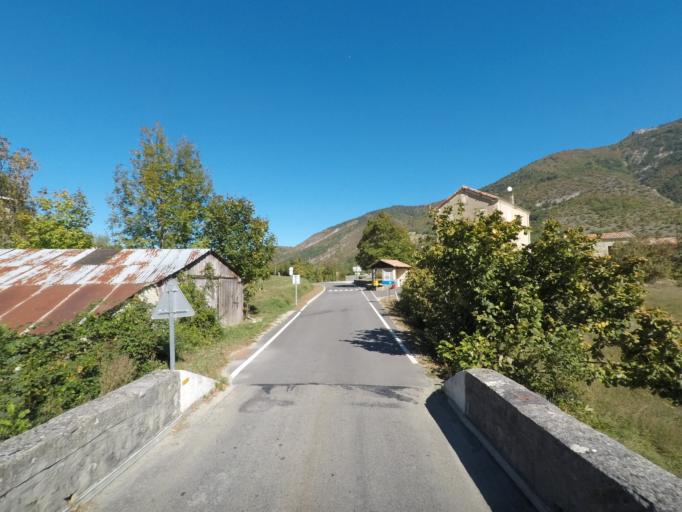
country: FR
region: Rhone-Alpes
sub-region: Departement de la Drome
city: Die
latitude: 44.6629
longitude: 5.2717
